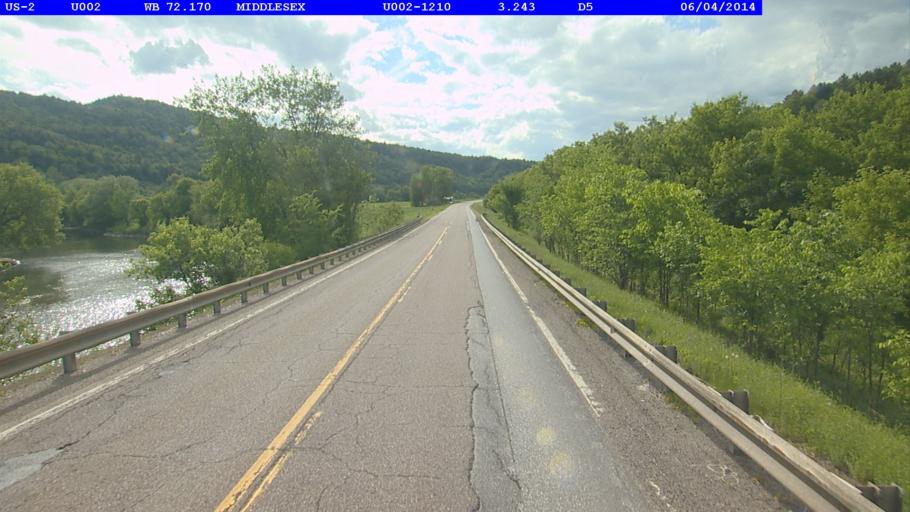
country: US
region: Vermont
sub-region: Washington County
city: Montpelier
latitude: 44.2761
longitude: -72.6516
